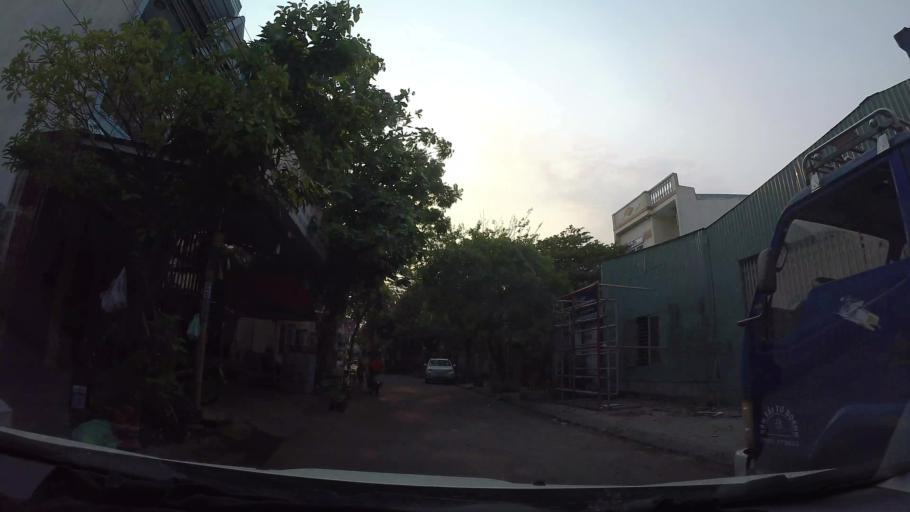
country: VN
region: Da Nang
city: Cam Le
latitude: 16.0210
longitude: 108.1957
